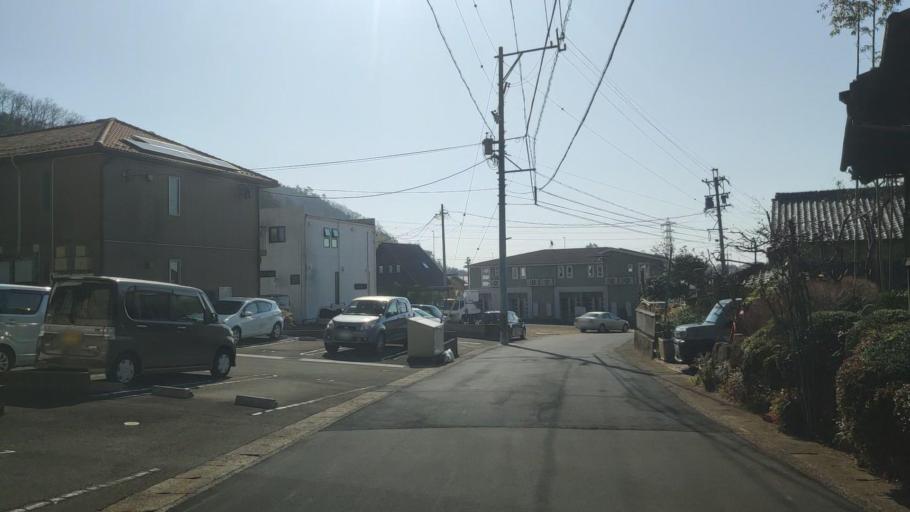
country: JP
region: Gifu
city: Gifu-shi
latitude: 35.4231
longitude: 136.7852
